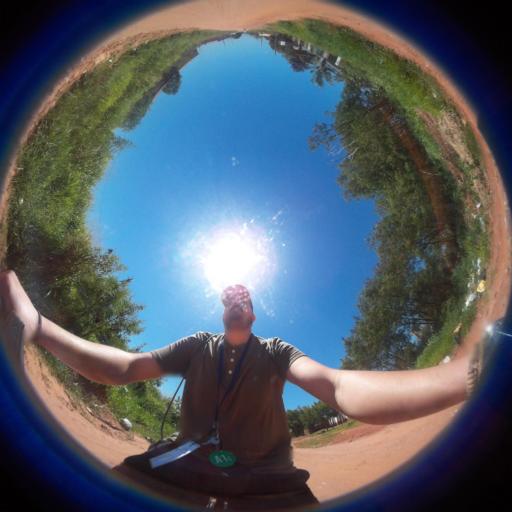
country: BR
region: Mato Grosso do Sul
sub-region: Ponta Pora
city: Ponta Pora
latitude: -22.5268
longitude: -55.7315
